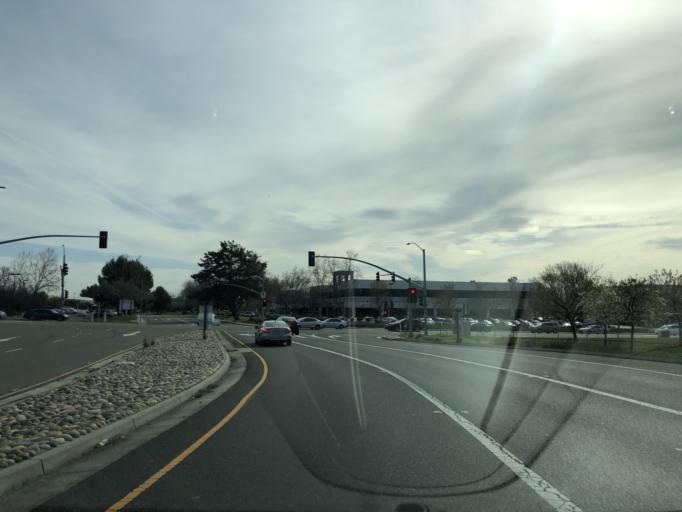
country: US
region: California
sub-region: Santa Clara County
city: Milpitas
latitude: 37.4838
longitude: -121.9392
